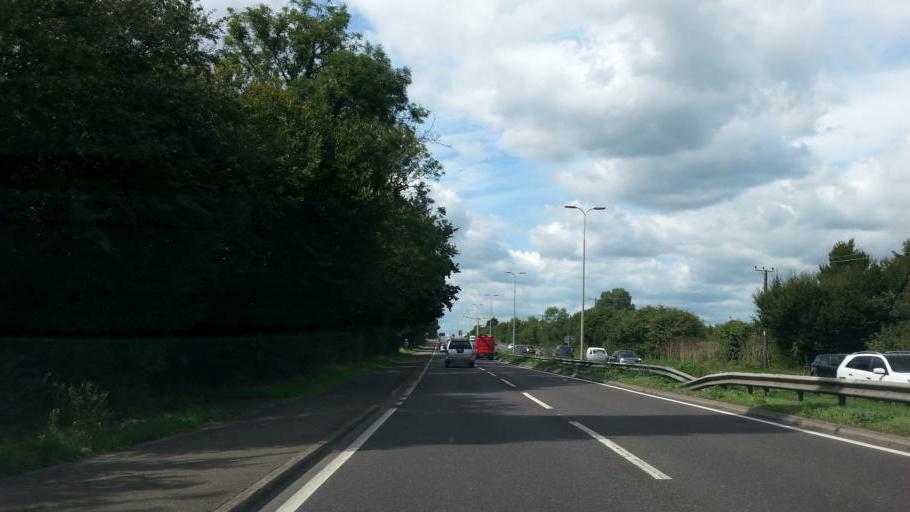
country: GB
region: England
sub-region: Essex
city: Wickford
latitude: 51.5890
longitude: 0.5506
